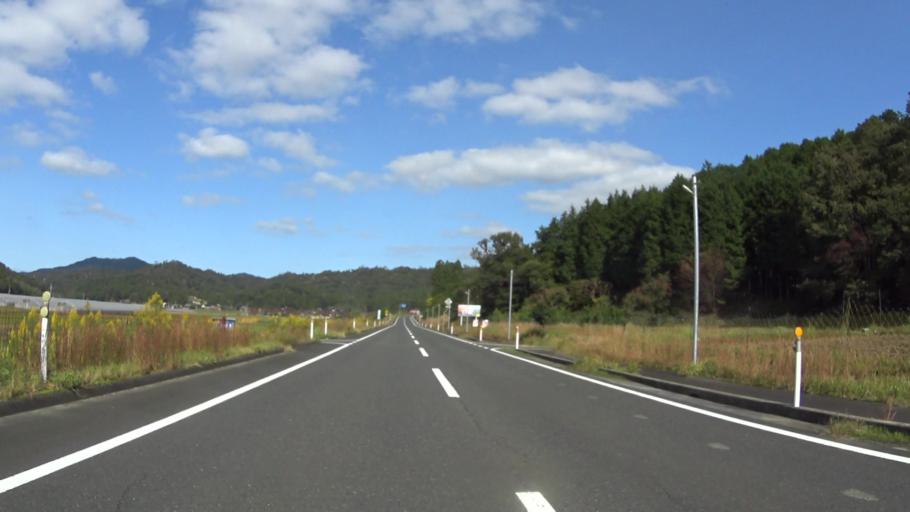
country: JP
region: Hyogo
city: Toyooka
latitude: 35.5683
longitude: 134.9750
